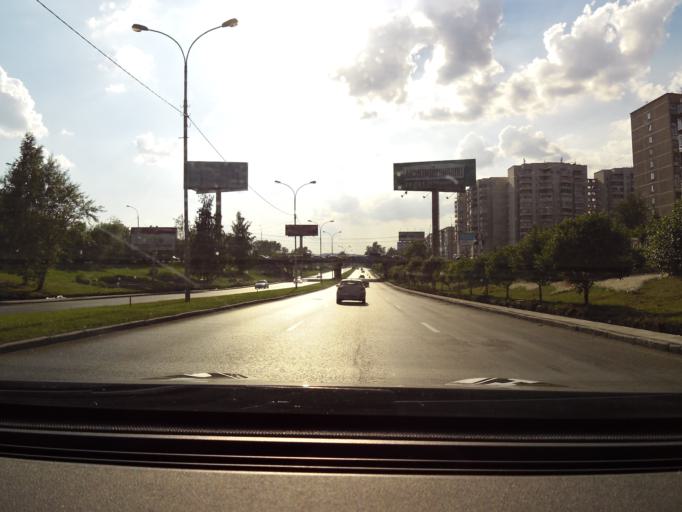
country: RU
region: Sverdlovsk
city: Sovkhoznyy
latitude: 56.8262
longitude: 60.5464
